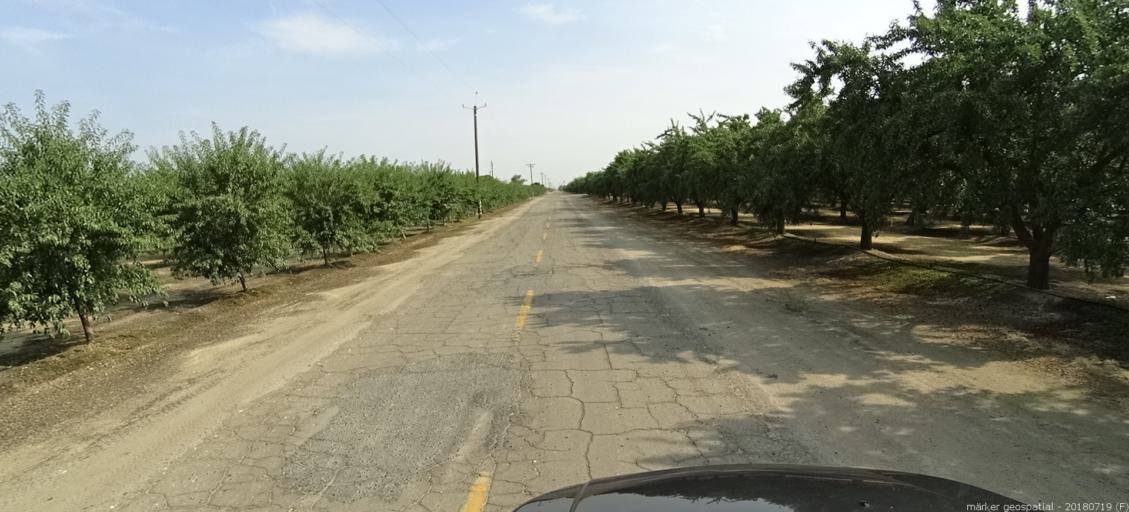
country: US
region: California
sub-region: Madera County
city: Fairmead
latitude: 37.0641
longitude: -120.1750
